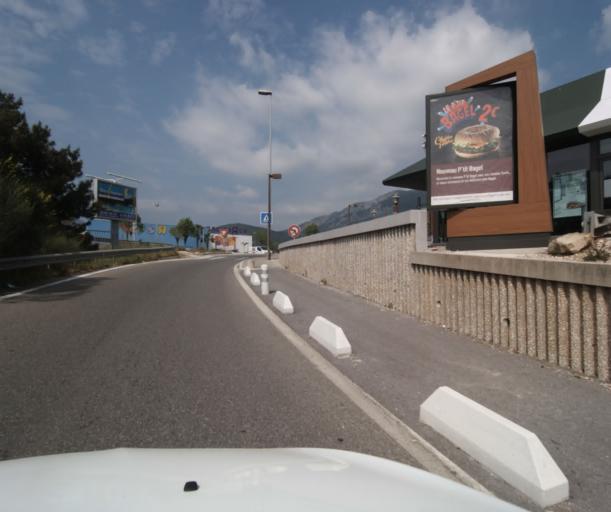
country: FR
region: Provence-Alpes-Cote d'Azur
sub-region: Departement du Var
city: La Garde
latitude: 43.1381
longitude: 6.0224
